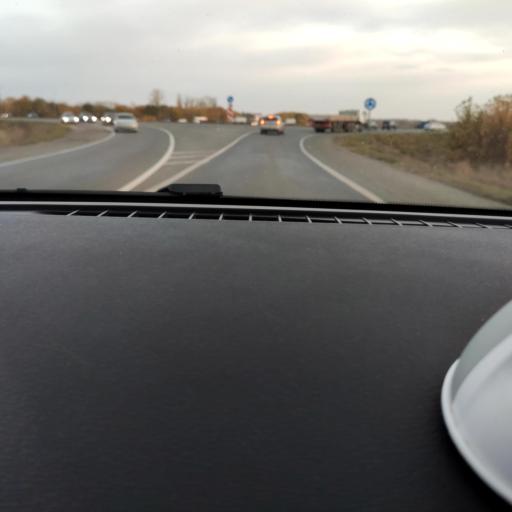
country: RU
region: Samara
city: Samara
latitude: 53.0935
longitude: 50.1495
